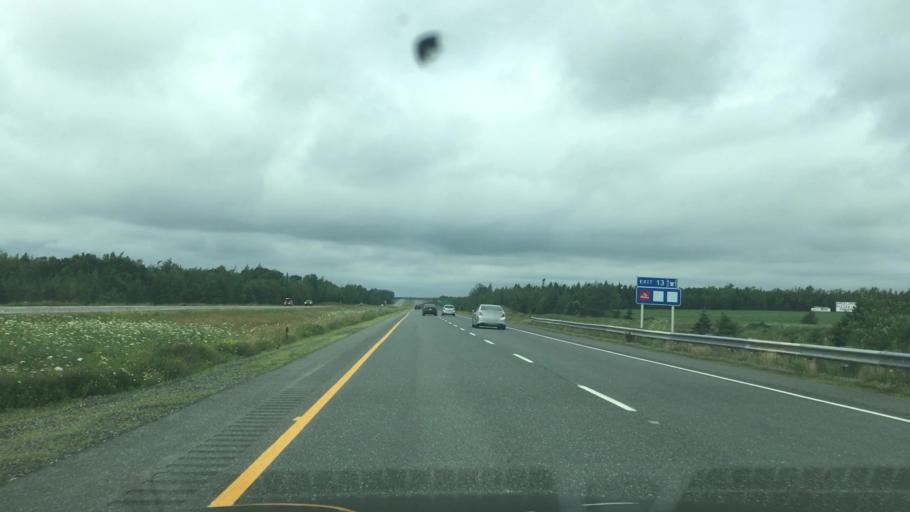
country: CA
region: Nova Scotia
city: Truro
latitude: 45.3845
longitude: -63.3711
